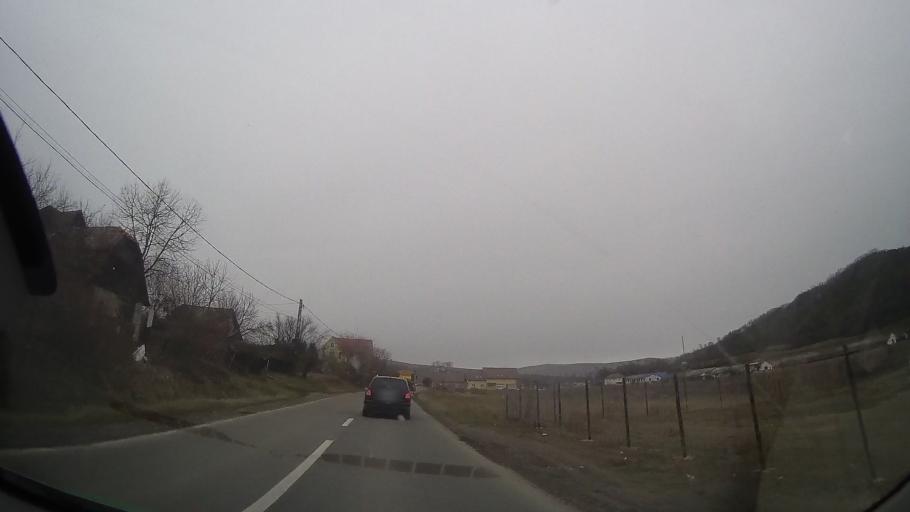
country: RO
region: Mures
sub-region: Comuna Ceausu de Campie
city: Ceausu de Campie
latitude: 46.6334
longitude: 24.5180
